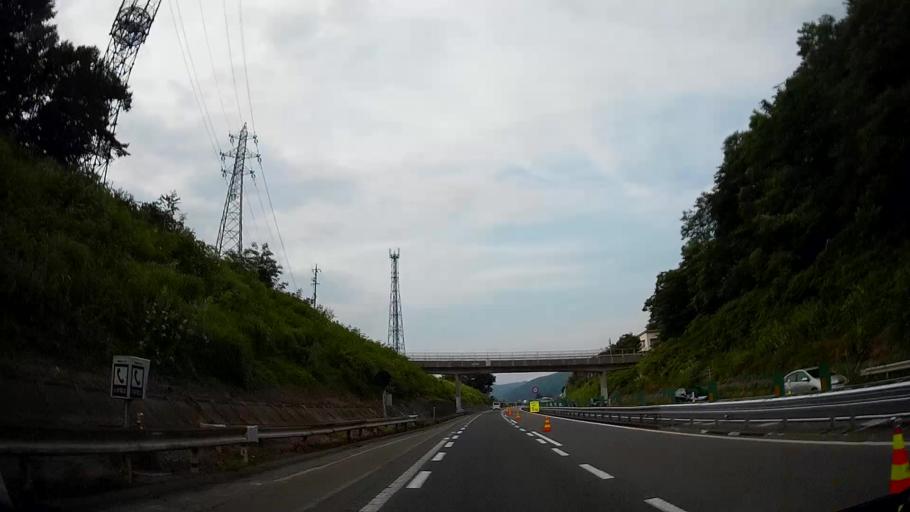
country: JP
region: Nagano
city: Tatsuno
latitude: 35.9683
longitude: 137.9964
